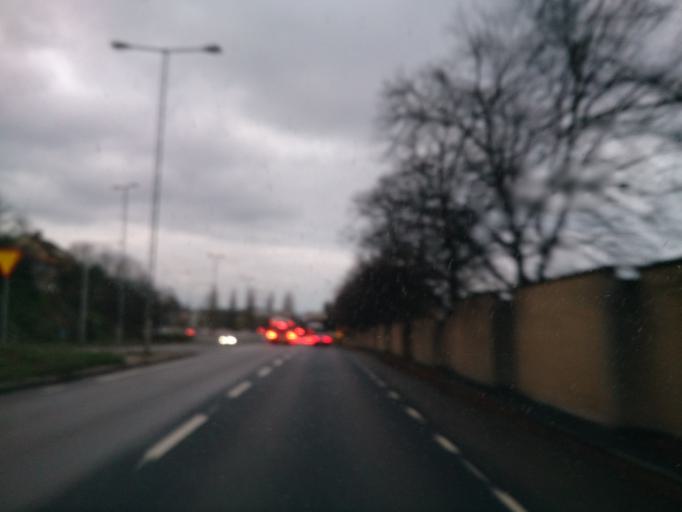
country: SE
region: OEstergoetland
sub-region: Linkopings Kommun
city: Linkoping
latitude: 58.4019
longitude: 15.6359
